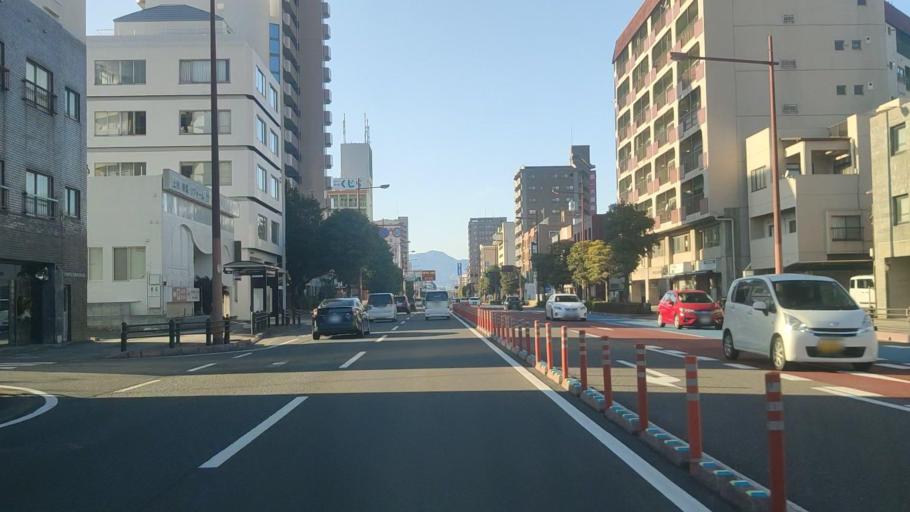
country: JP
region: Oita
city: Oita
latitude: 33.2395
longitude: 131.5970
